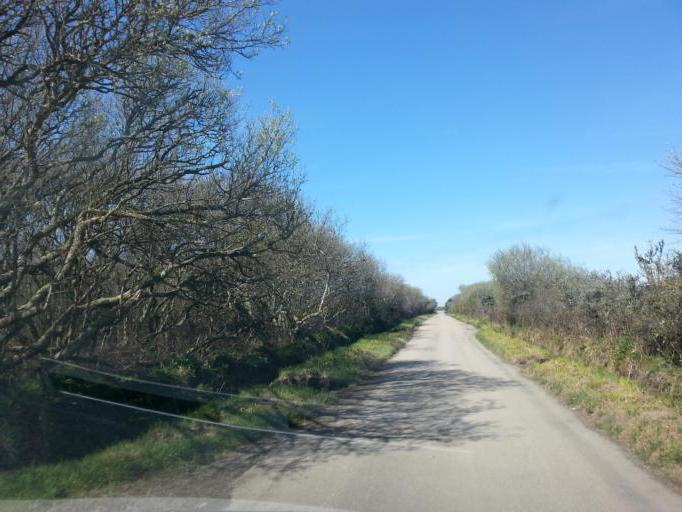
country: GB
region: England
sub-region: Cornwall
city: Landewednack
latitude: 49.9906
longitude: -5.2056
